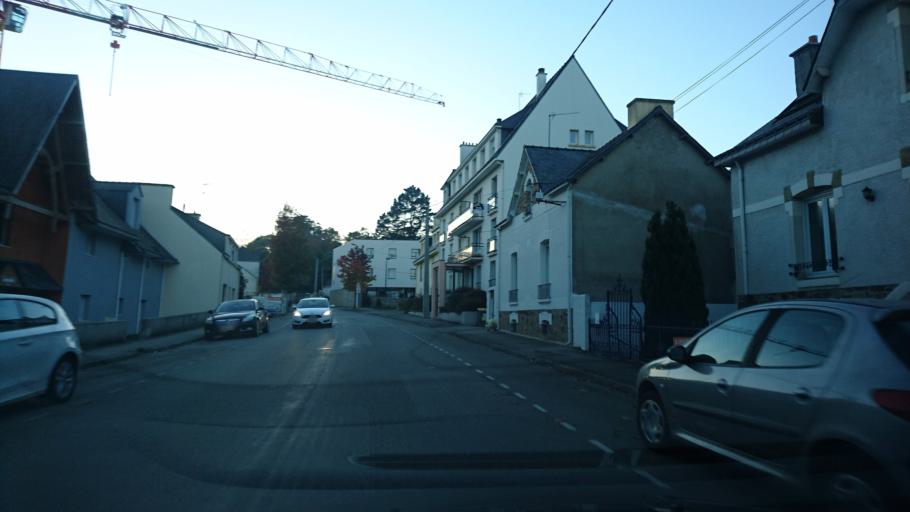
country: FR
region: Brittany
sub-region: Departement du Morbihan
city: Auray
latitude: 47.6687
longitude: -2.9764
